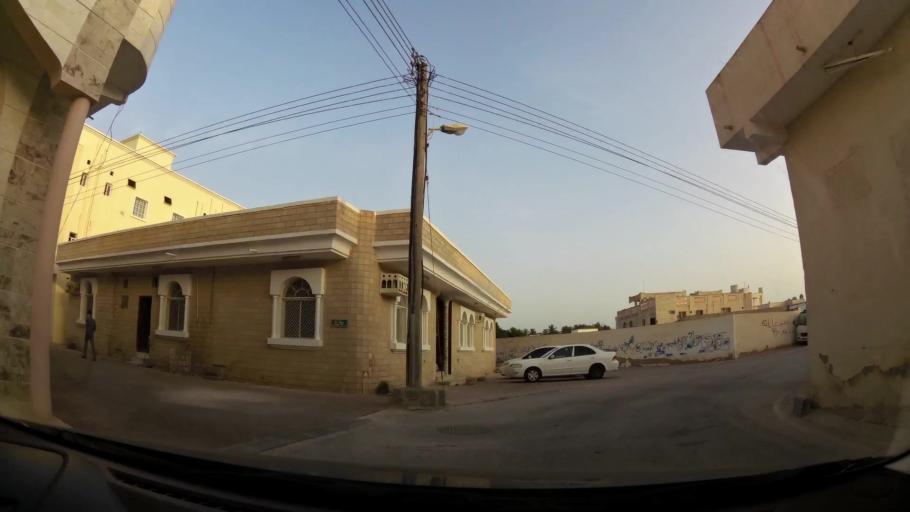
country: OM
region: Zufar
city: Salalah
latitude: 17.0179
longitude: 54.1154
